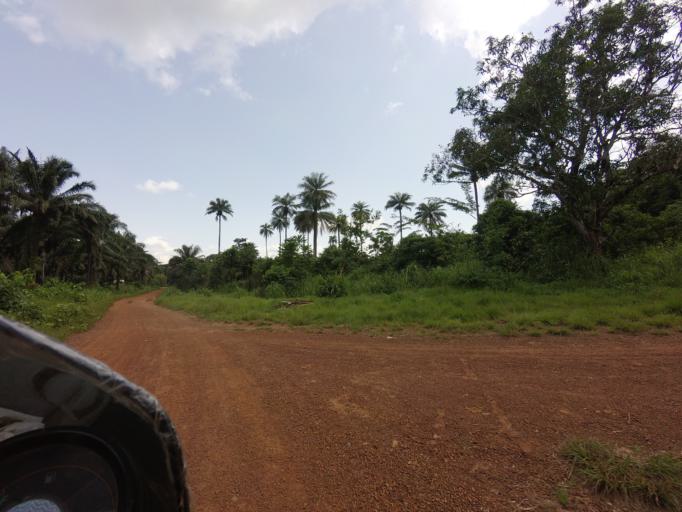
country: SL
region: Eastern Province
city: Manowa
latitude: 8.1472
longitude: -10.7756
